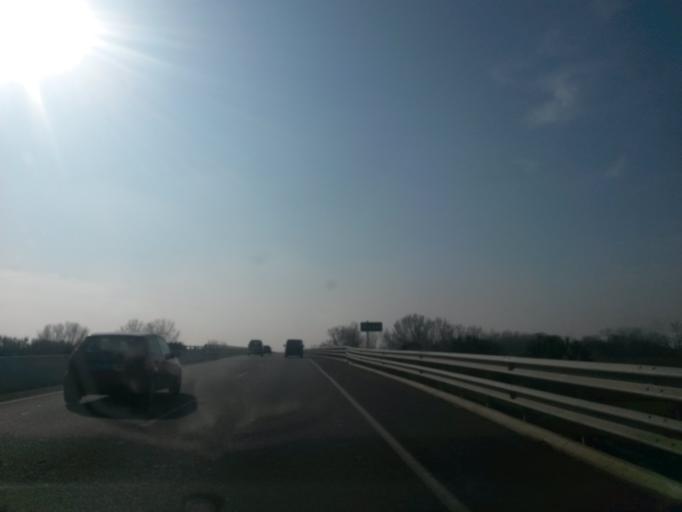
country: ES
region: Catalonia
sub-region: Provincia de Girona
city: Castello d'Empuries
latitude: 42.2565
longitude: 3.0877
